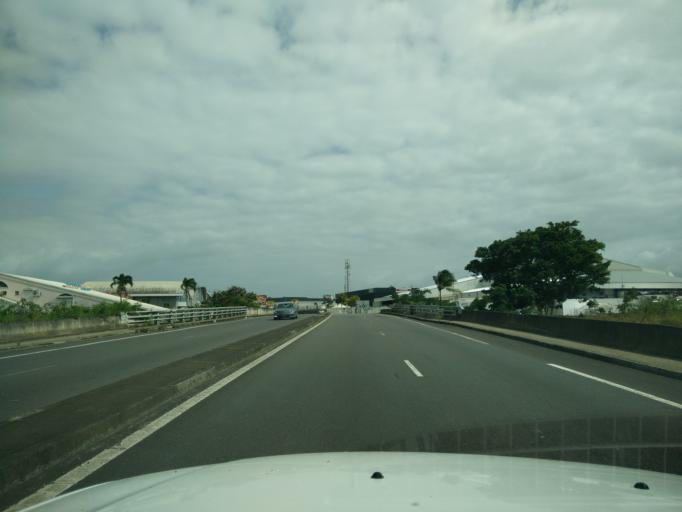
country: GP
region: Guadeloupe
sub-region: Guadeloupe
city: Baie-Mahault
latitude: 16.2444
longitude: -61.5718
